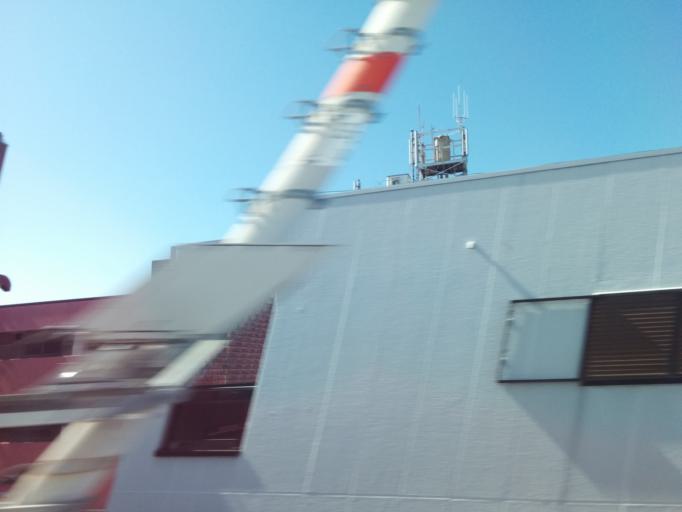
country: JP
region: Aichi
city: Nagoya-shi
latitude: 35.1242
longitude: 136.8878
